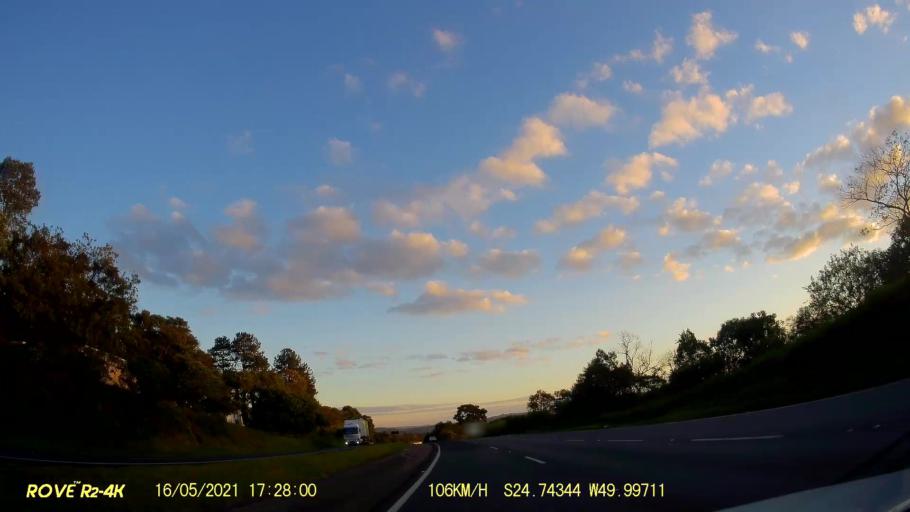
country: BR
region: Parana
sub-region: Castro
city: Castro
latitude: -24.7437
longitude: -49.9972
